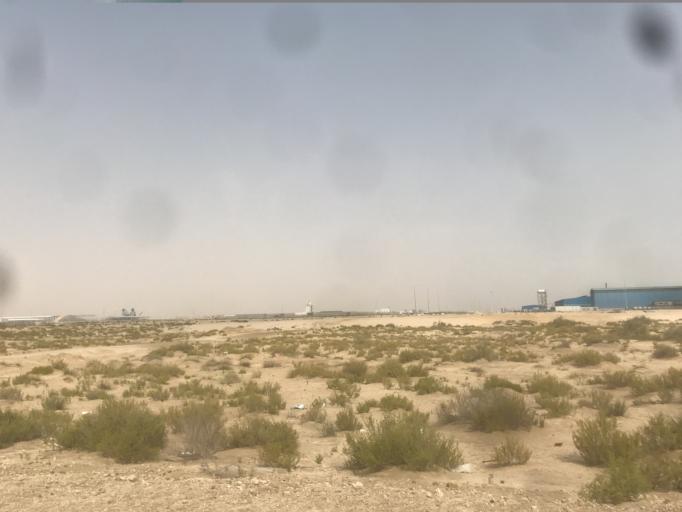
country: SA
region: Eastern Province
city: Abqaiq
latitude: 25.9106
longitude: 49.9537
